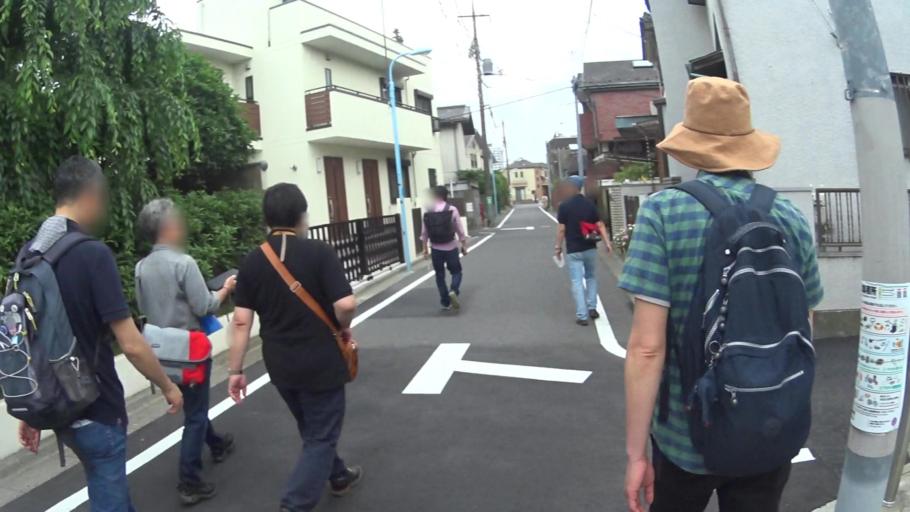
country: JP
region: Tokyo
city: Musashino
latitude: 35.7119
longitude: 139.6195
